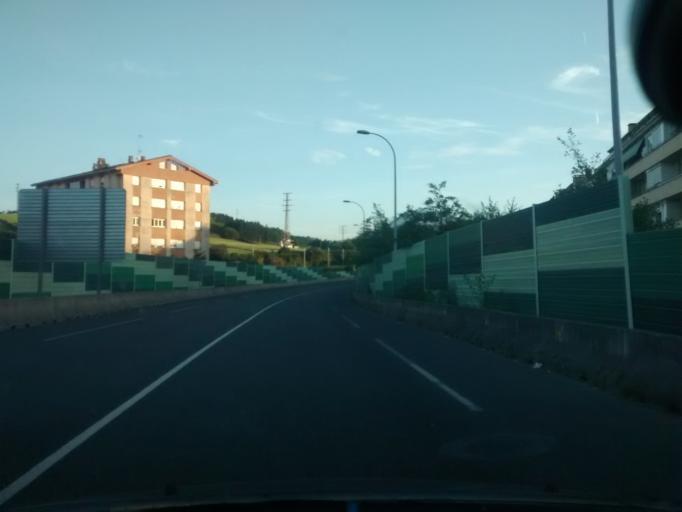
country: ES
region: Basque Country
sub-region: Provincia de Guipuzcoa
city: Zumaia
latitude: 43.2927
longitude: -2.2531
